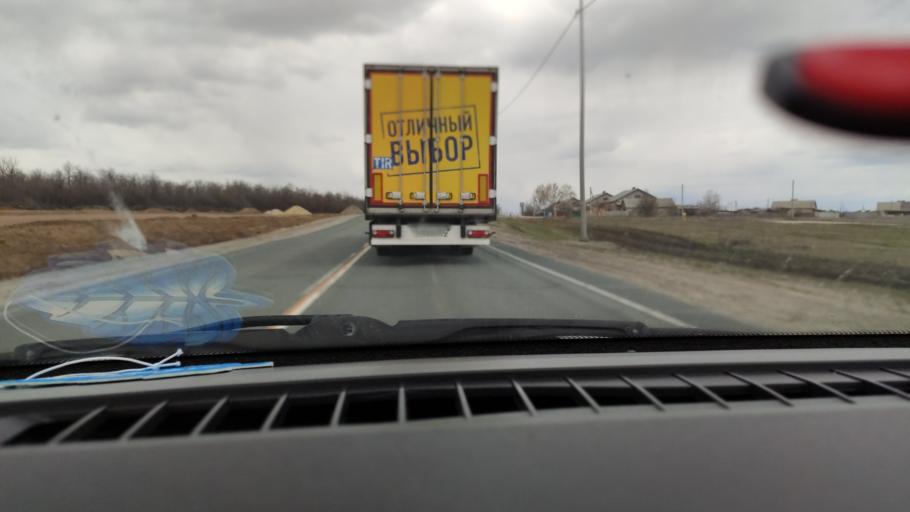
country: RU
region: Saratov
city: Sennoy
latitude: 52.1589
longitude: 47.0620
